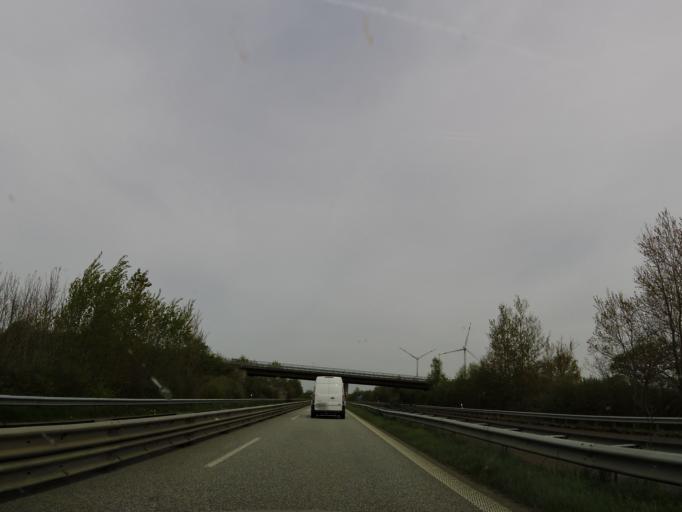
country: DE
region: Schleswig-Holstein
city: Tensbuttel-Rost
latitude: 54.1270
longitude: 9.2552
